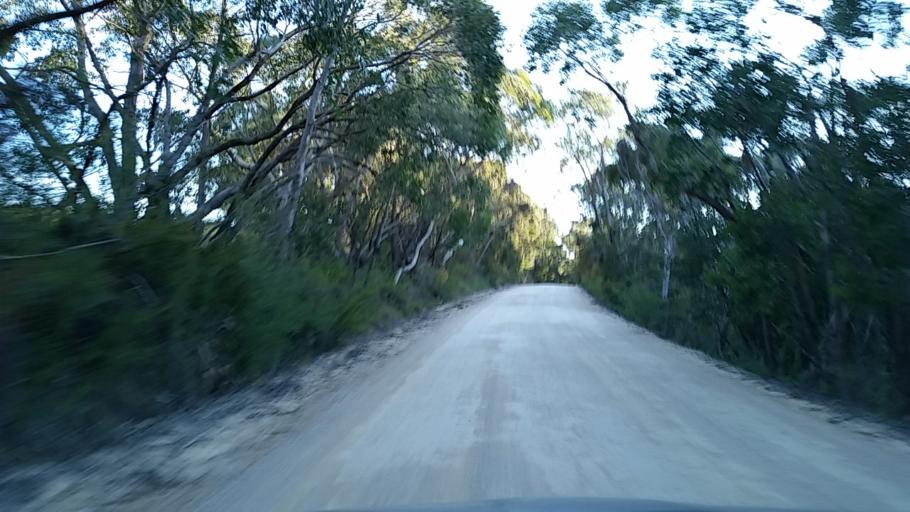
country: AU
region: South Australia
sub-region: Alexandrina
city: Mount Compass
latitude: -35.2983
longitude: 138.6829
